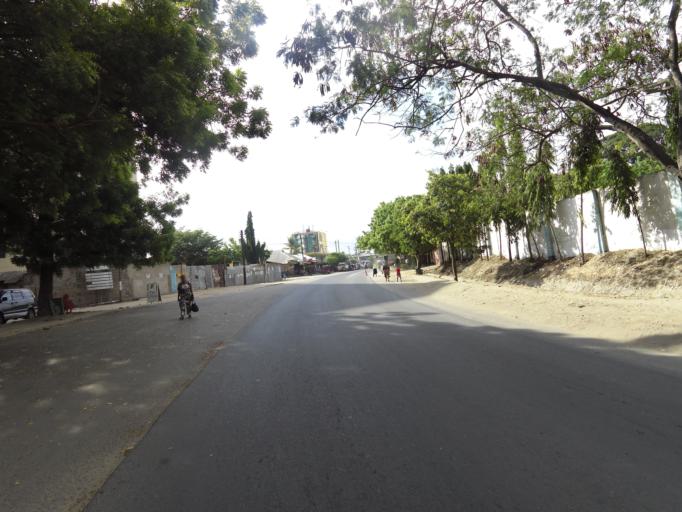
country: TZ
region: Dar es Salaam
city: Magomeni
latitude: -6.7729
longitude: 39.2334
